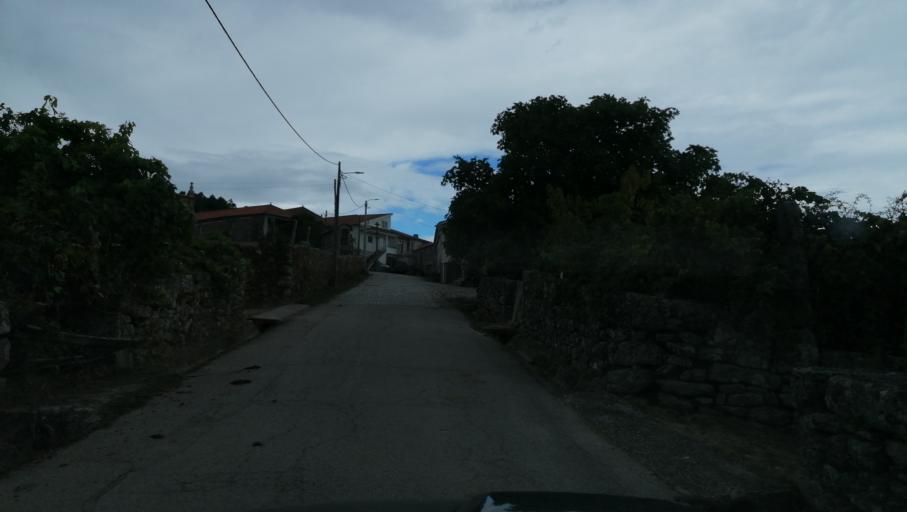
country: PT
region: Vila Real
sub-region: Vila Pouca de Aguiar
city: Vila Pouca de Aguiar
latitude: 41.5613
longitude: -7.6524
